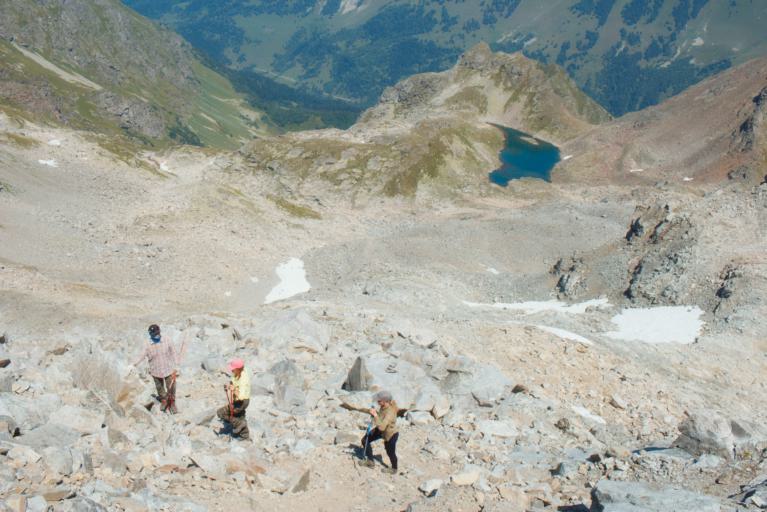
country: RU
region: Karachayevo-Cherkesiya
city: Nizhniy Arkhyz
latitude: 43.4533
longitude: 41.2175
